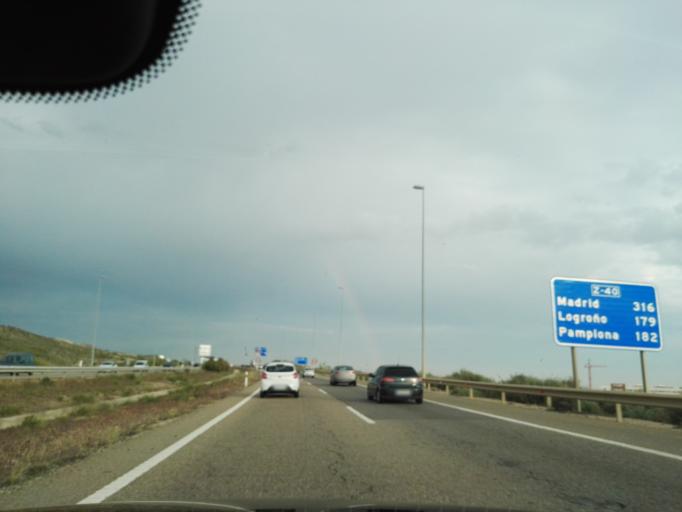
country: ES
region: Aragon
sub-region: Provincia de Zaragoza
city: Montecanal
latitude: 41.6186
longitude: -0.9425
